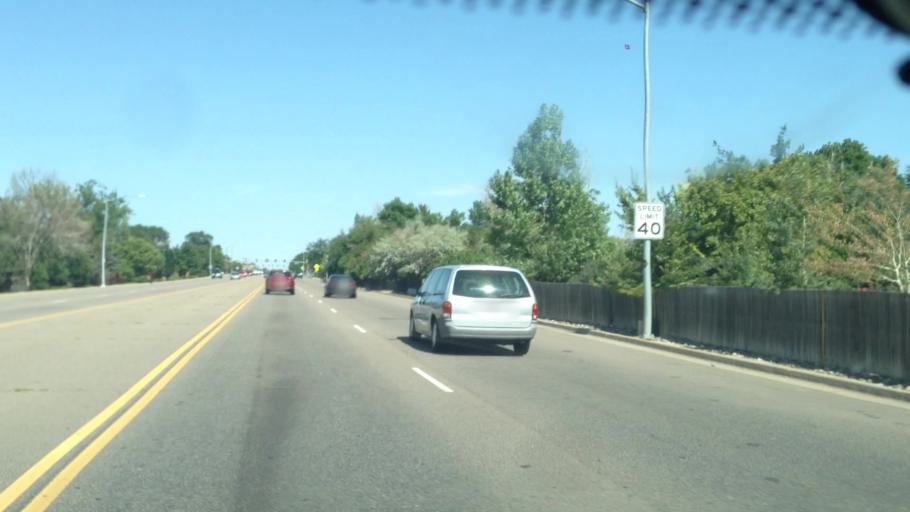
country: US
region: Colorado
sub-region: Adams County
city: Aurora
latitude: 39.7256
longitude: -104.8554
